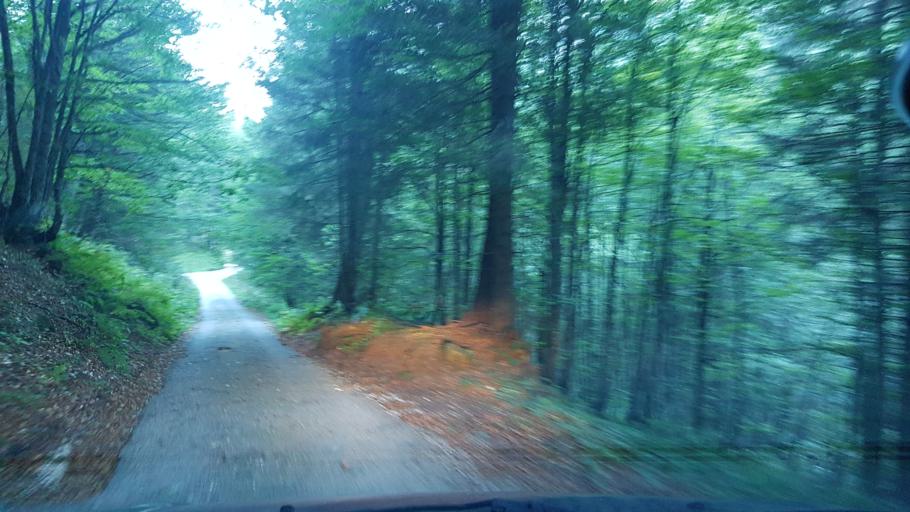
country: IT
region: Veneto
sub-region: Provincia di Belluno
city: Fusine
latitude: 46.3552
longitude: 12.0906
